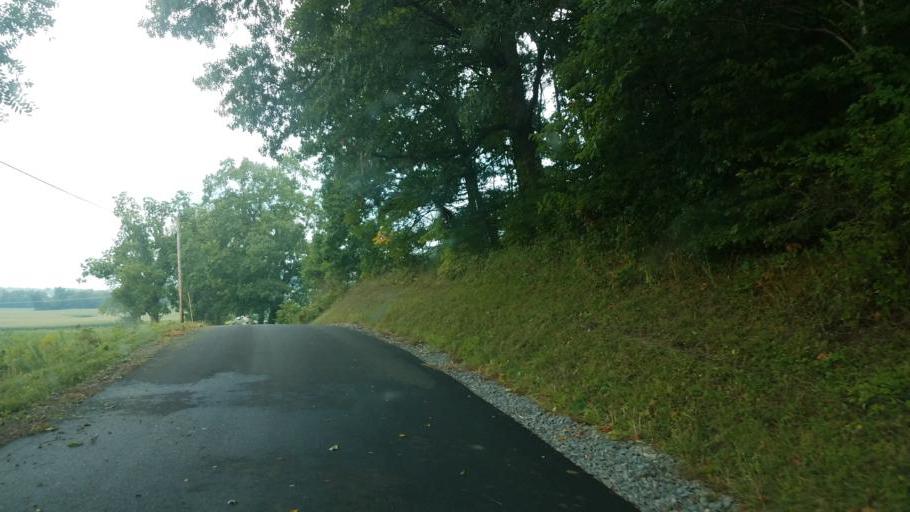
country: US
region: Ohio
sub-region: Licking County
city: Utica
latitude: 40.2075
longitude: -82.4631
